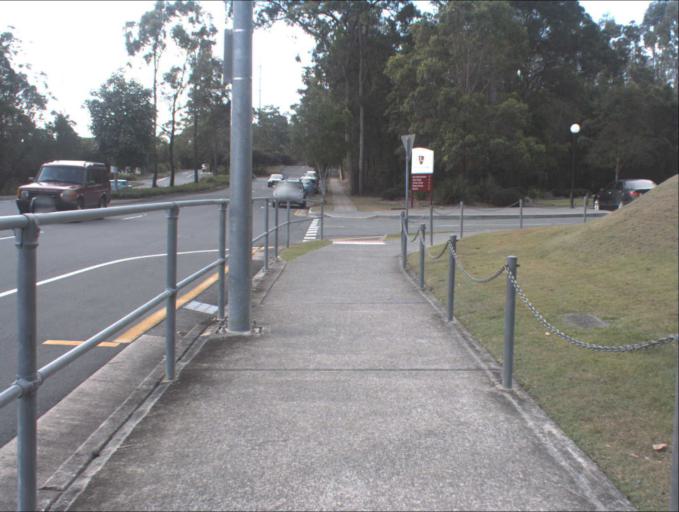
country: AU
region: Queensland
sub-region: Logan
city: Slacks Creek
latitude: -27.6338
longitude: 153.1485
